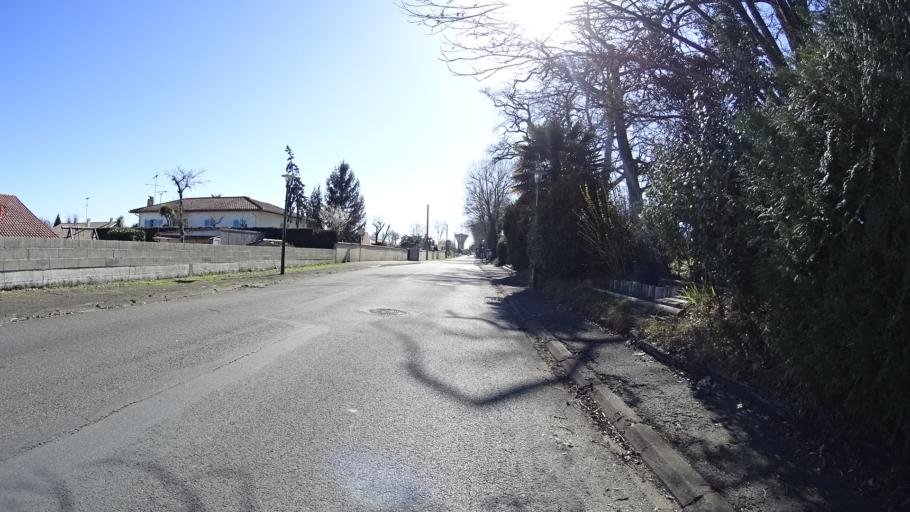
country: FR
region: Aquitaine
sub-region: Departement des Landes
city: Saint-Paul-les-Dax
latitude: 43.7316
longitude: -1.0861
